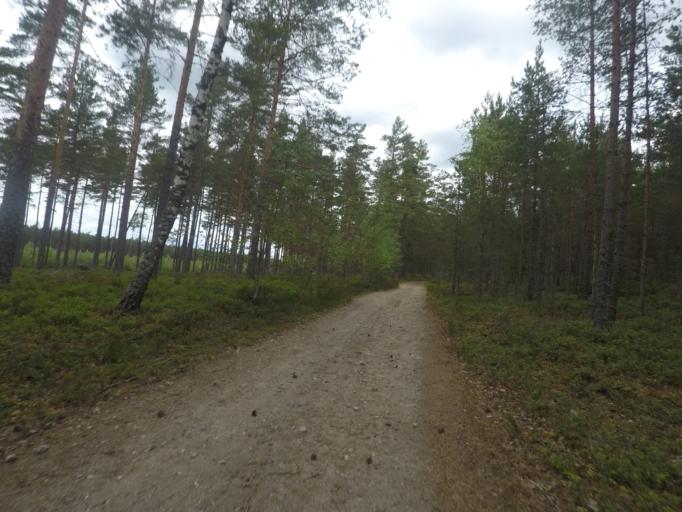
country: SE
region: Vaestmanland
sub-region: Kungsors Kommun
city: Kungsoer
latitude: 59.3672
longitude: 16.1078
